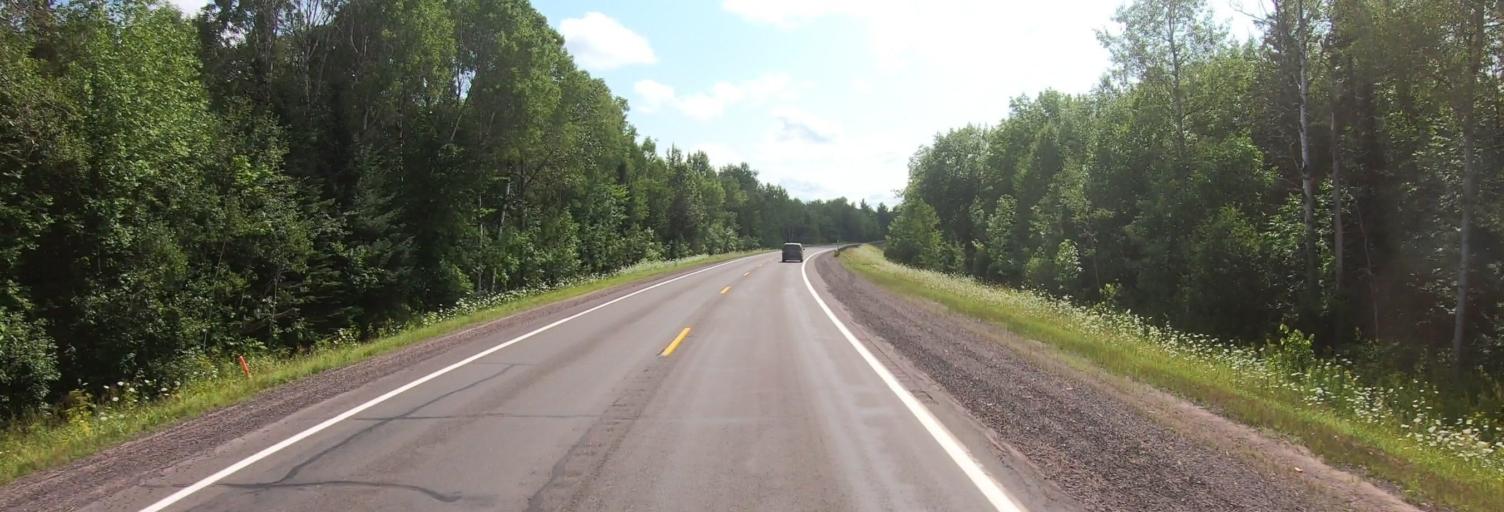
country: US
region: Michigan
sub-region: Ontonagon County
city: Ontonagon
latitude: 46.7429
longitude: -89.1061
